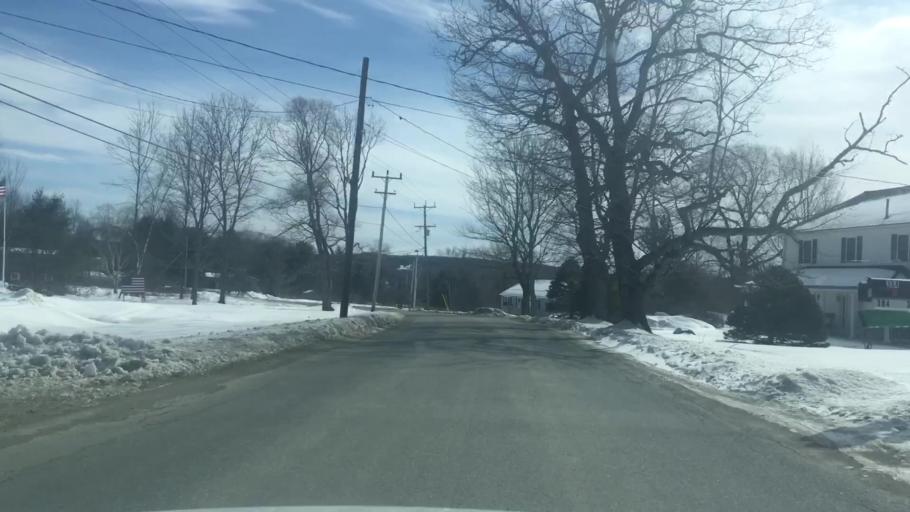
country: US
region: Maine
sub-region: Penobscot County
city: Eddington
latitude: 44.7994
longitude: -68.6789
